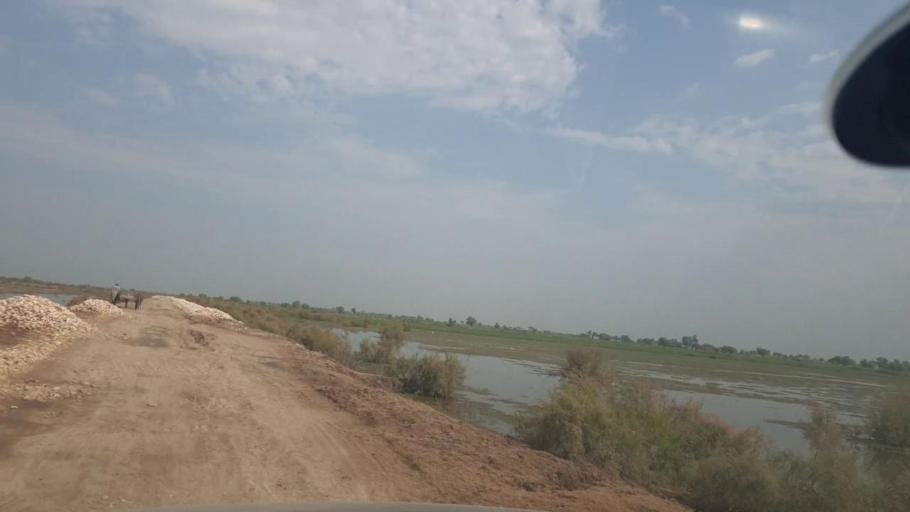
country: PK
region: Balochistan
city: Mehrabpur
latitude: 28.0834
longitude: 68.0994
